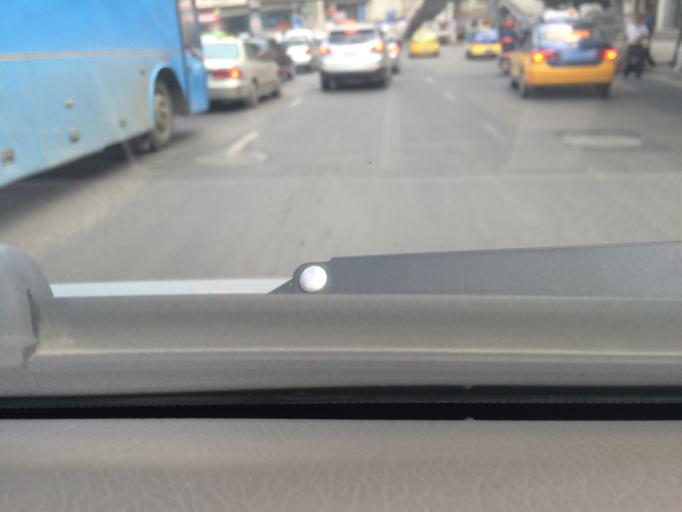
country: CN
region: Guizhou Sheng
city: Guiyang
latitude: 26.5836
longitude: 106.6804
